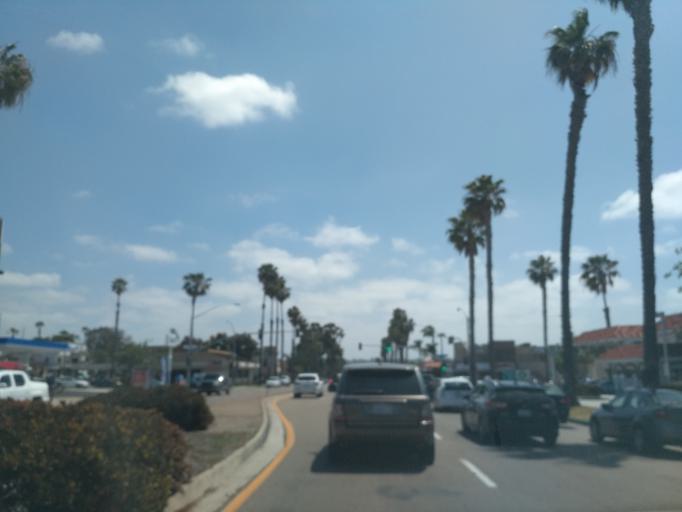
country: US
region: California
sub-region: San Diego County
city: La Jolla
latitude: 32.7976
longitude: -117.2413
